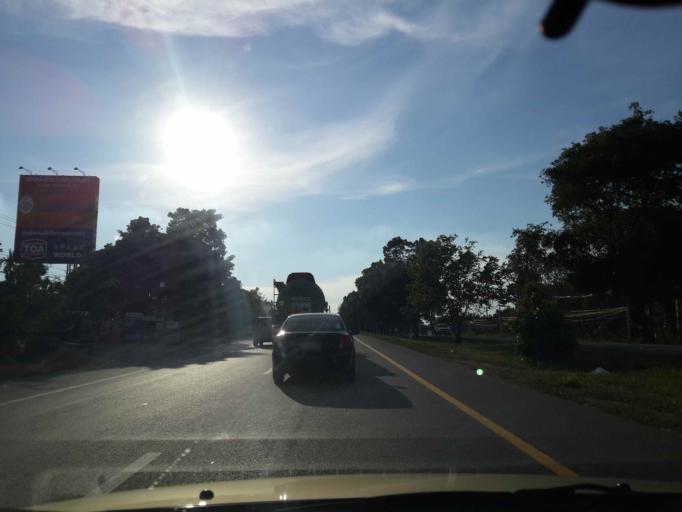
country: TH
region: Chon Buri
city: Bang Lamung
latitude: 12.9824
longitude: 100.9542
